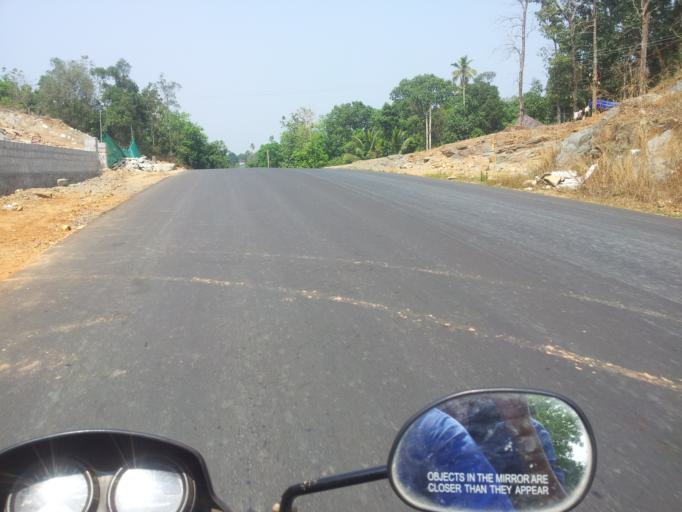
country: IN
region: Kerala
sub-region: Ernakulam
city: Muvattupuzha
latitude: 9.8914
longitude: 76.6974
